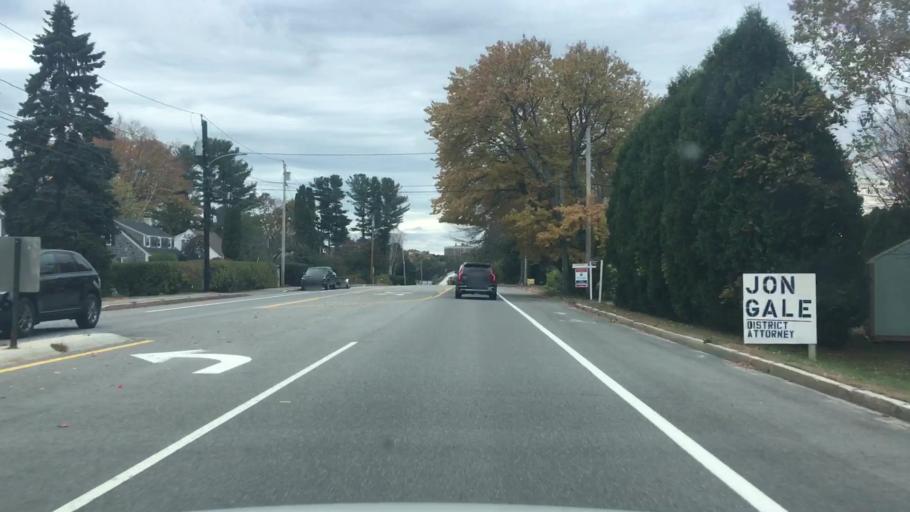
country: US
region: Maine
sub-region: Cumberland County
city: Falmouth
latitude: 43.6967
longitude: -70.2421
